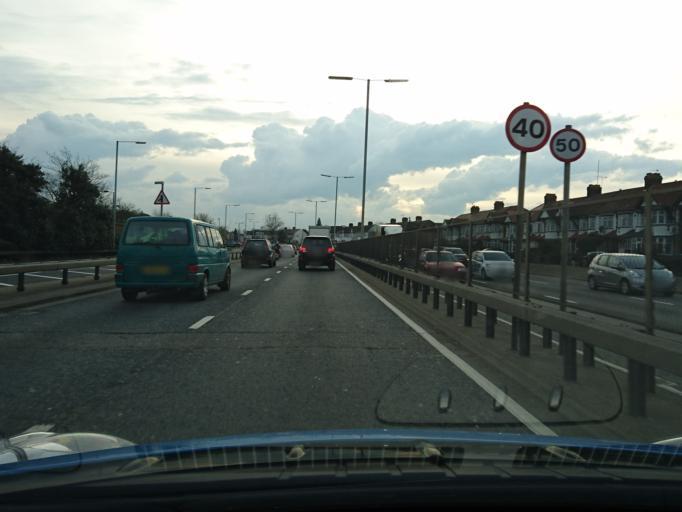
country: GB
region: England
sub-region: Greater London
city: Wood Green
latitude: 51.6162
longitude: -0.0937
